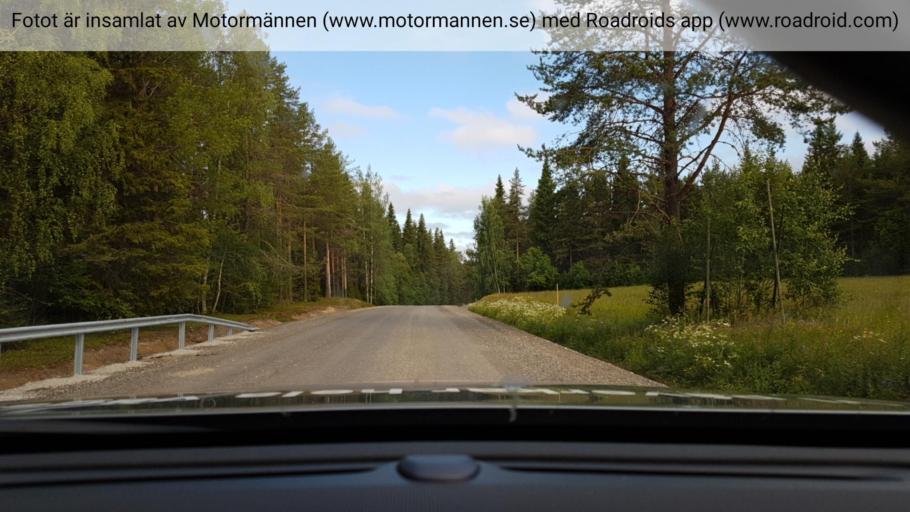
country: SE
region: Vaesterbotten
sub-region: Norsjo Kommun
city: Norsjoe
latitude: 64.6459
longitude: 19.2831
